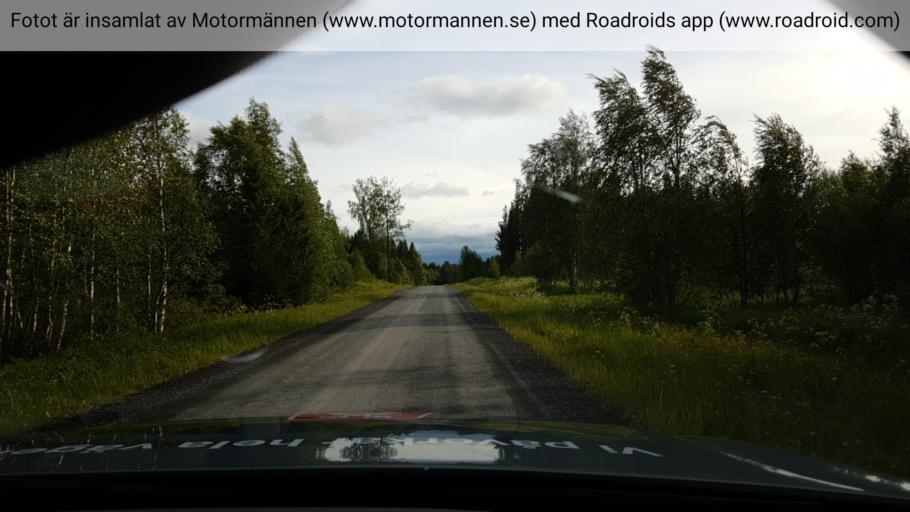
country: SE
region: Jaemtland
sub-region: Stroemsunds Kommun
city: Stroemsund
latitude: 63.7046
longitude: 15.1737
